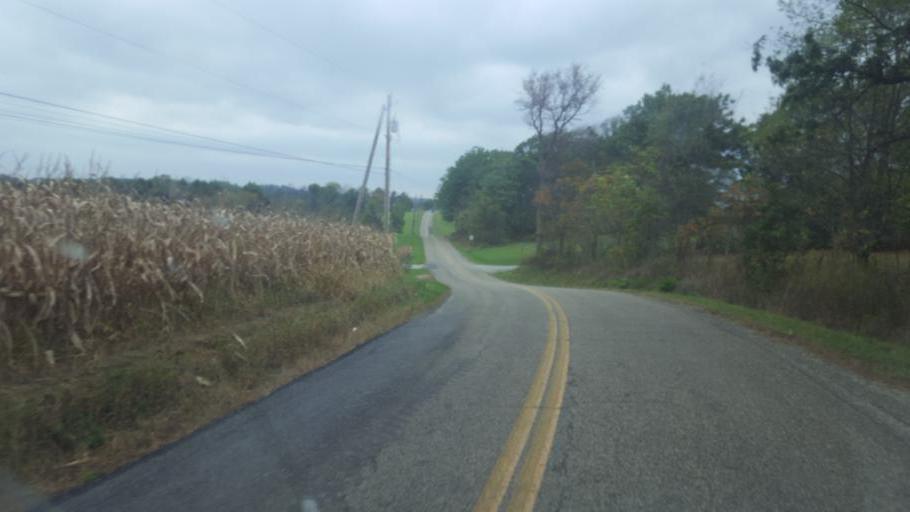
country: US
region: Ohio
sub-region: Carroll County
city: Carrollton
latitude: 40.5342
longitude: -81.1571
